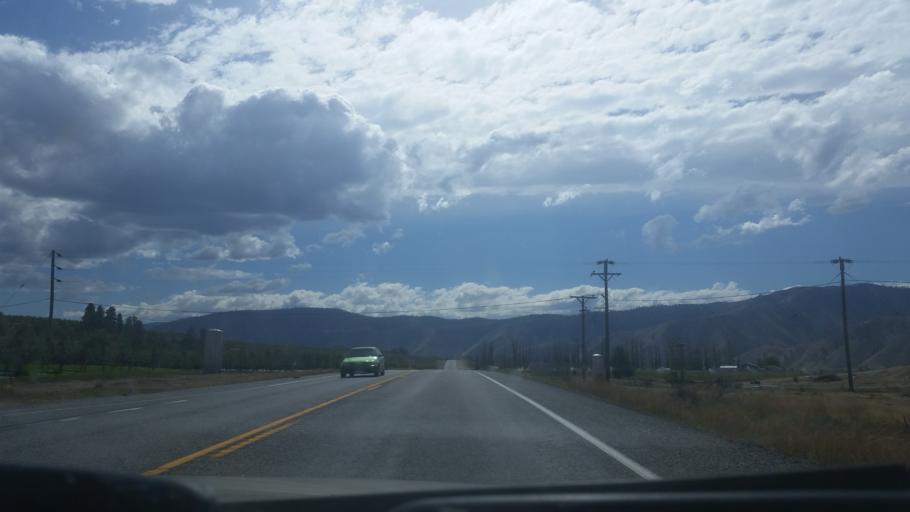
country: US
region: Washington
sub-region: Chelan County
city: Entiat
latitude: 47.7597
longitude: -120.1564
